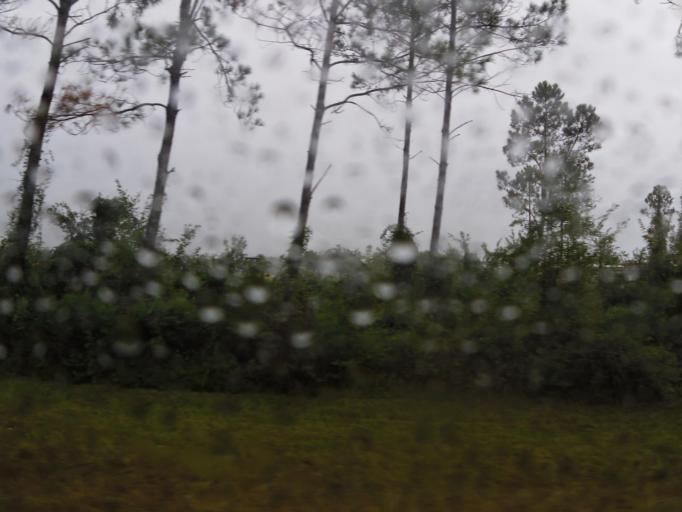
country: US
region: Florida
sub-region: Baker County
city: Macclenny
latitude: 30.3707
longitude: -82.1394
